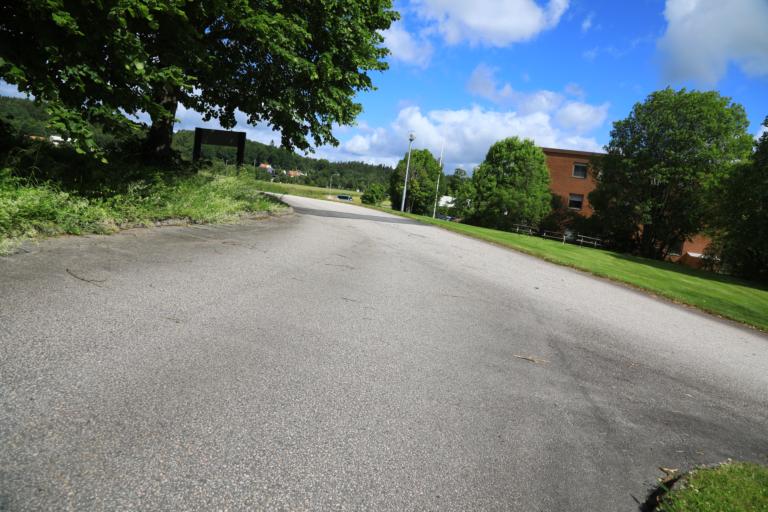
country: SE
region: Vaestra Goetaland
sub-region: Marks Kommun
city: Kinna
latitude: 57.5149
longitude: 12.7149
